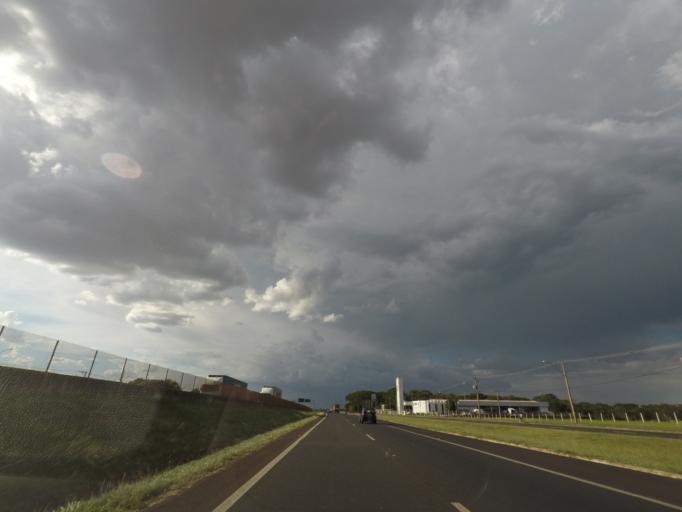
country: BR
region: Sao Paulo
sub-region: Ribeirao Preto
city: Ribeirao Preto
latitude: -21.1433
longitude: -47.7601
